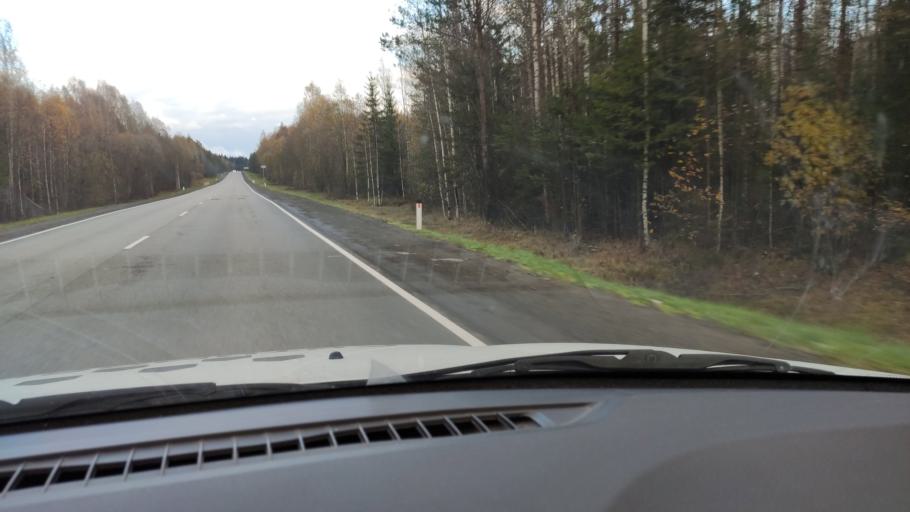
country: RU
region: Kirov
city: Belaya Kholunitsa
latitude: 58.8998
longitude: 50.9287
